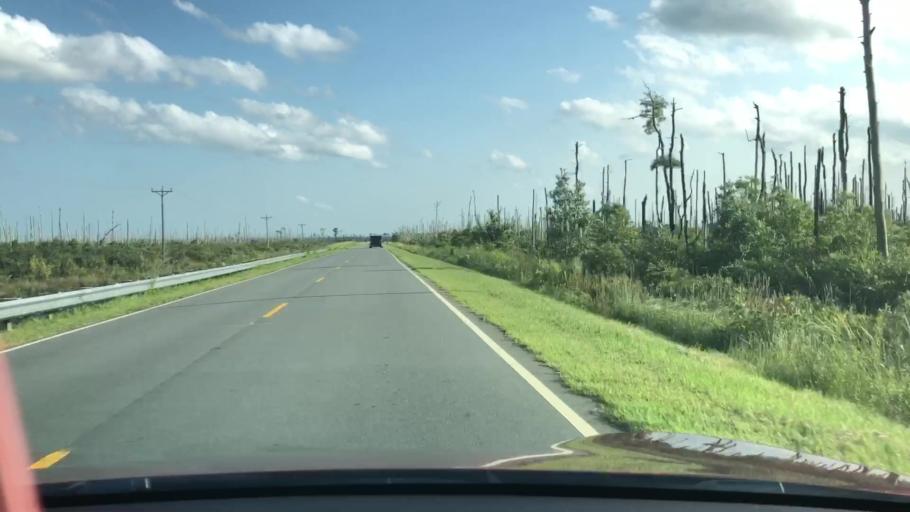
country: US
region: North Carolina
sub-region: Dare County
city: Wanchese
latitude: 35.6528
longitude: -75.7773
